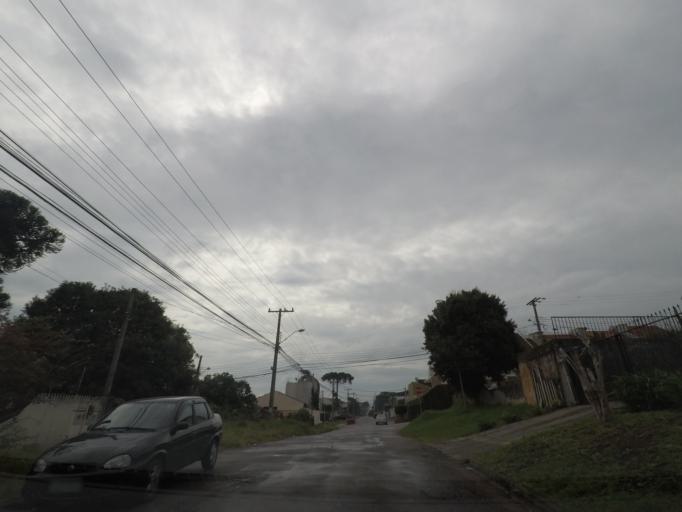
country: BR
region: Parana
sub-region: Curitiba
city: Curitiba
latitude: -25.4691
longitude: -49.3096
